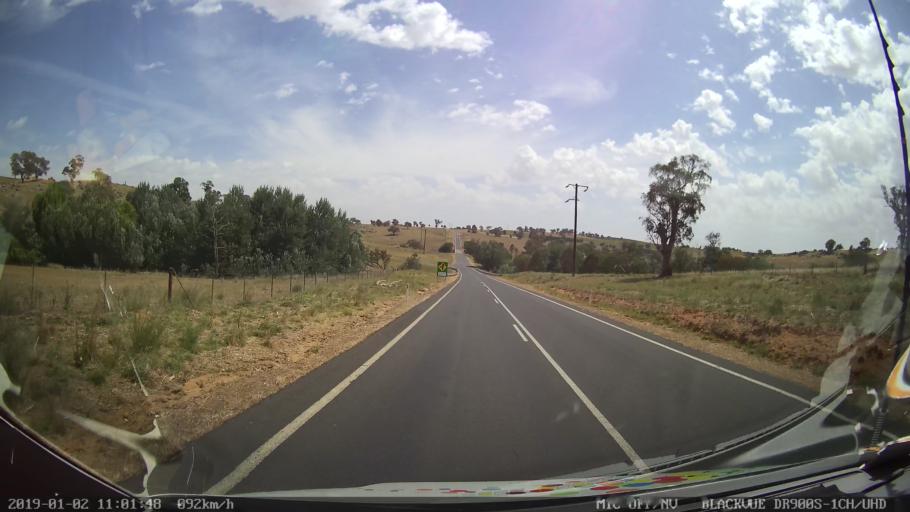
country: AU
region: New South Wales
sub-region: Young
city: Young
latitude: -34.5937
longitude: 148.3224
